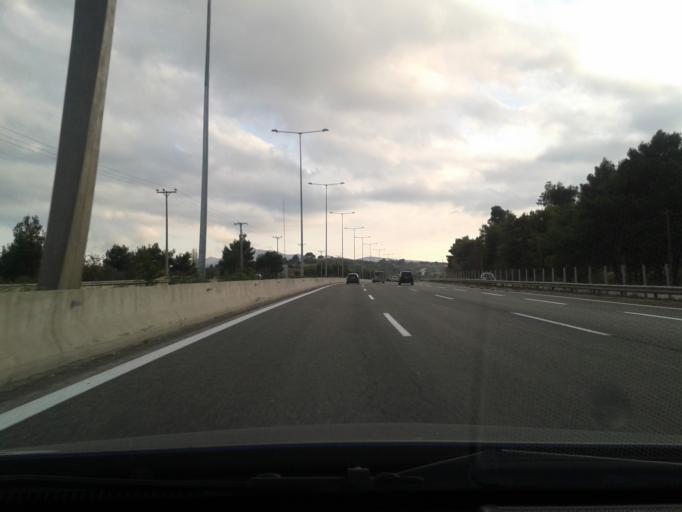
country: GR
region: Attica
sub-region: Nomarchia Anatolikis Attikis
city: Agios Stefanos
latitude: 38.1677
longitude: 23.8562
